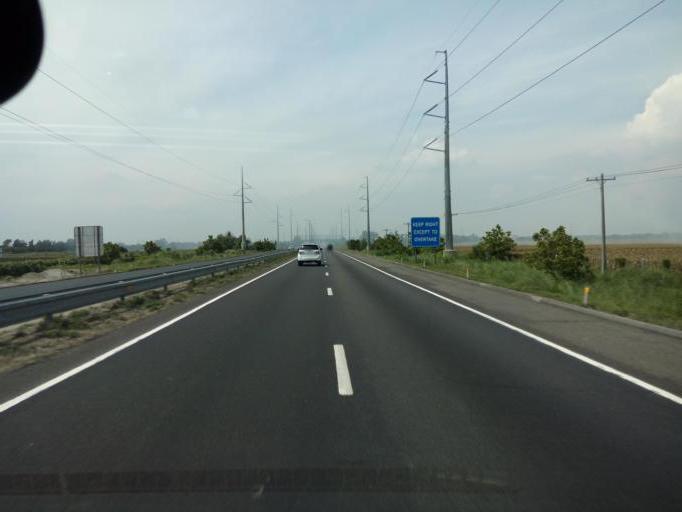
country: PH
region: Central Luzon
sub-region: Province of Tarlac
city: Santo Nino
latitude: 15.3091
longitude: 120.6187
